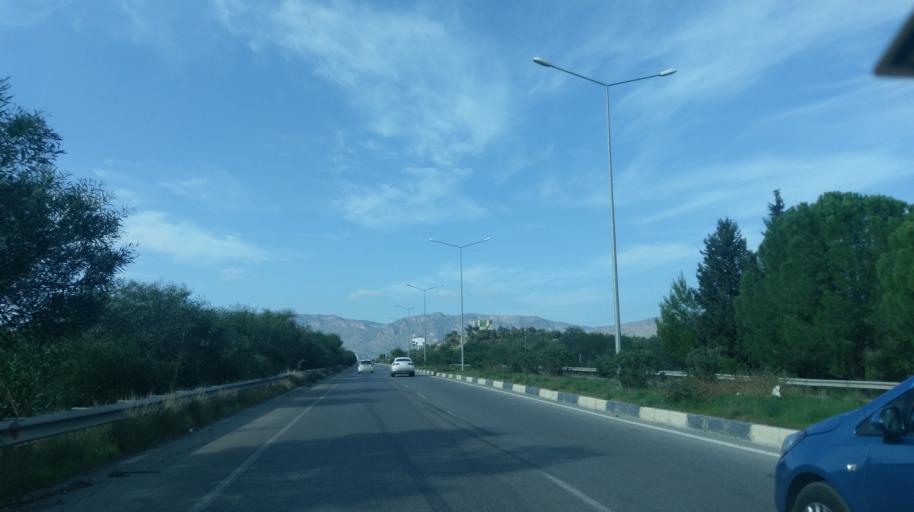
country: CY
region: Keryneia
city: Kyrenia
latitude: 35.2472
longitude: 33.3060
